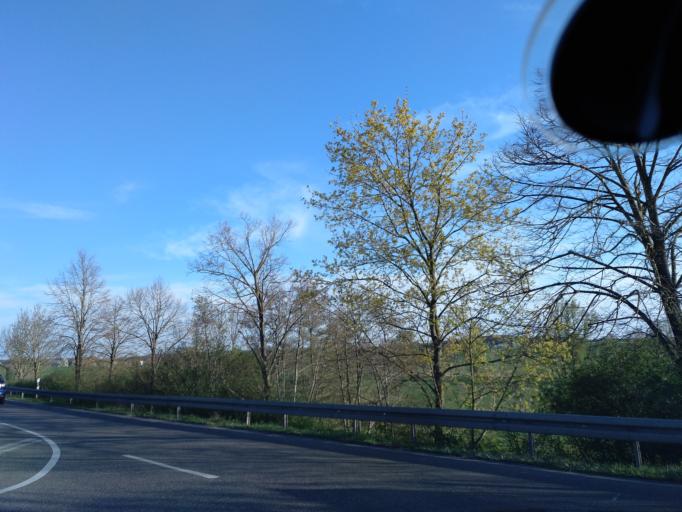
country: DE
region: Baden-Wuerttemberg
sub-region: Regierungsbezirk Stuttgart
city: Ilshofen
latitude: 49.1642
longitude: 9.9525
